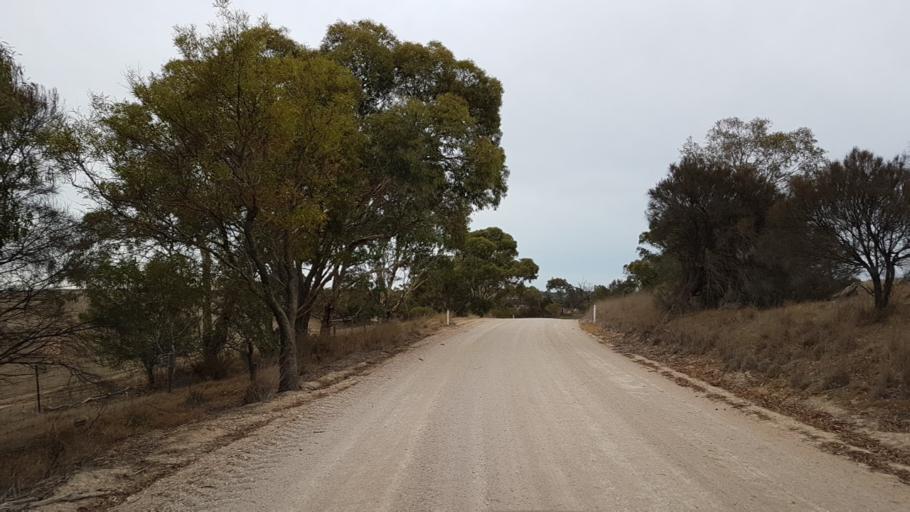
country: AU
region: South Australia
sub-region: Mount Barker
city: Nairne
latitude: -35.0020
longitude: 139.0057
